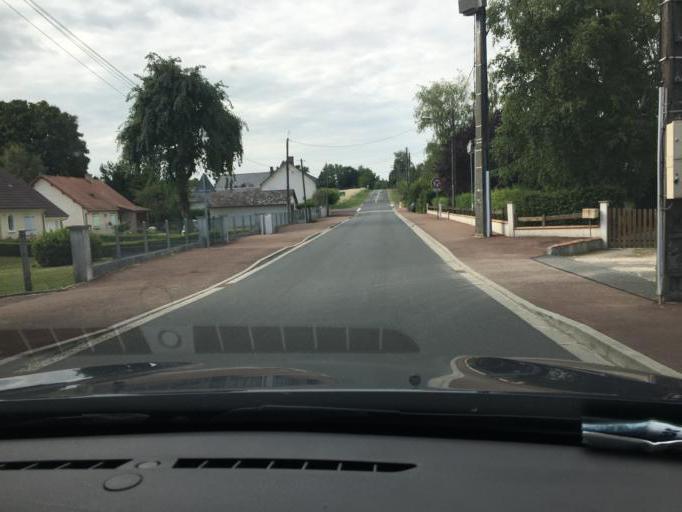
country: FR
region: Centre
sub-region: Departement du Cher
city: Rians
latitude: 47.2015
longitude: 2.5710
